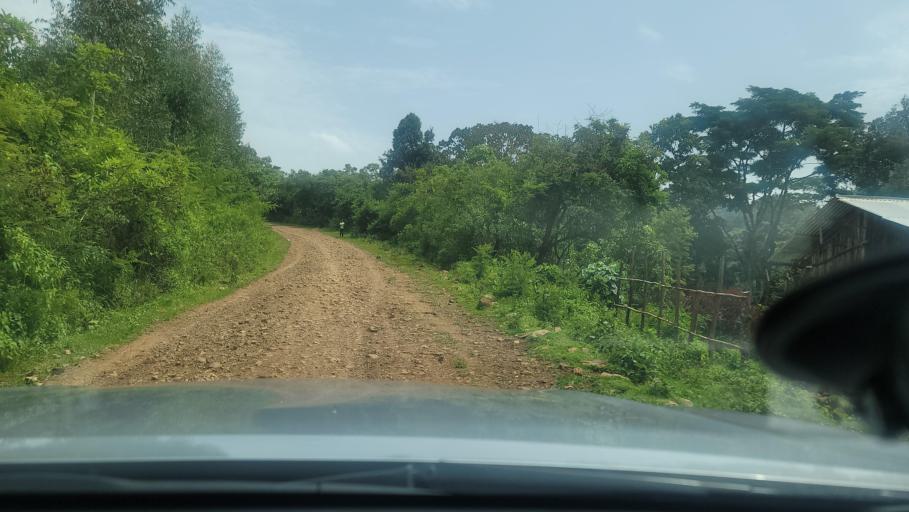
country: ET
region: Oromiya
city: Agaro
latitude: 7.8012
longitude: 36.4174
